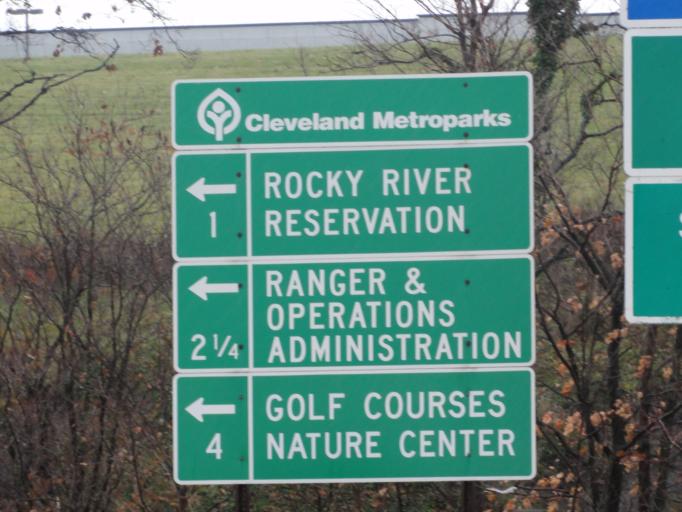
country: US
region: Ohio
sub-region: Cuyahoga County
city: Fairview Park
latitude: 41.4247
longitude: -81.8439
